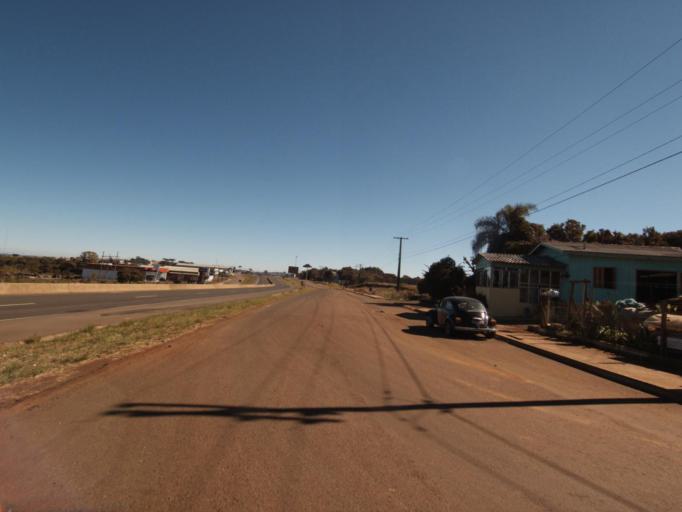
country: BR
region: Santa Catarina
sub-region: Xanxere
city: Xanxere
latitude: -26.8813
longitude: -52.3750
